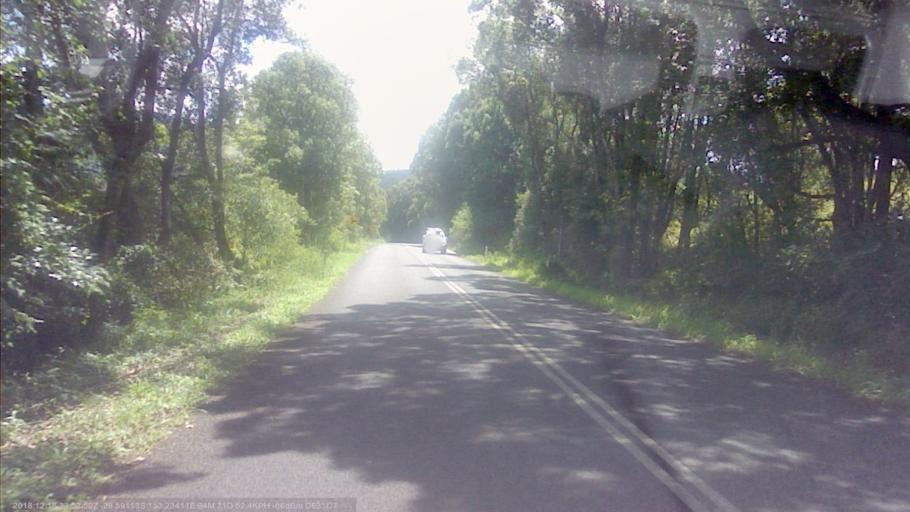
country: AU
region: New South Wales
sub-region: Lismore Municipality
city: Nimbin
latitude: -28.5911
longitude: 153.2341
